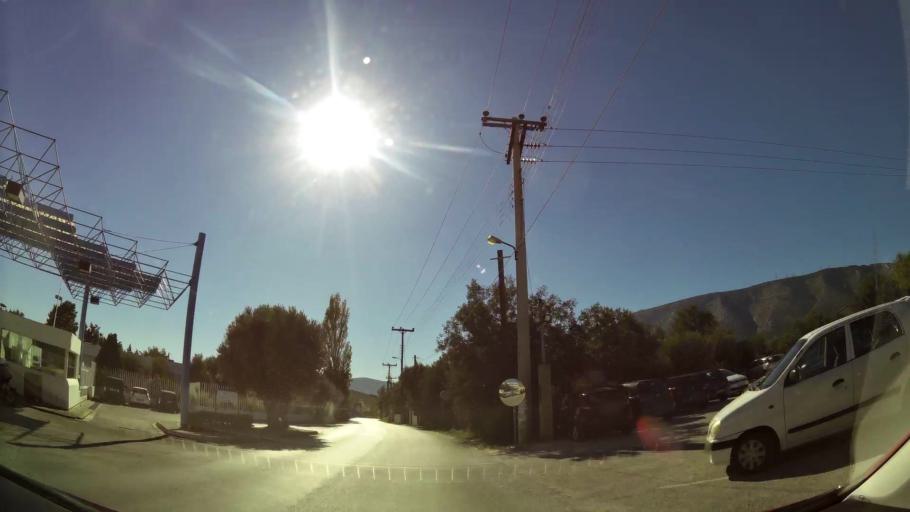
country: GR
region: Attica
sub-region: Nomarchia Anatolikis Attikis
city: Paiania
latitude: 37.9578
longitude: 23.8617
